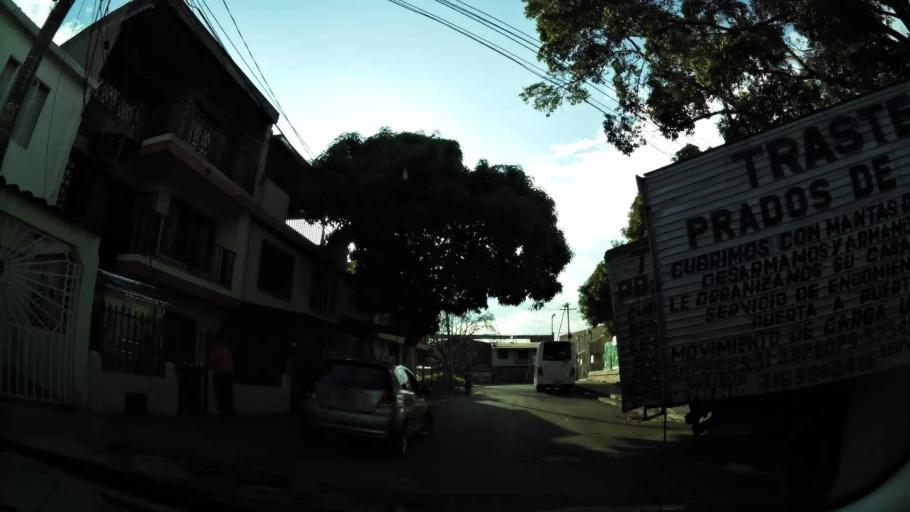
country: CO
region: Valle del Cauca
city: Cali
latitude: 3.4337
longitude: -76.5157
